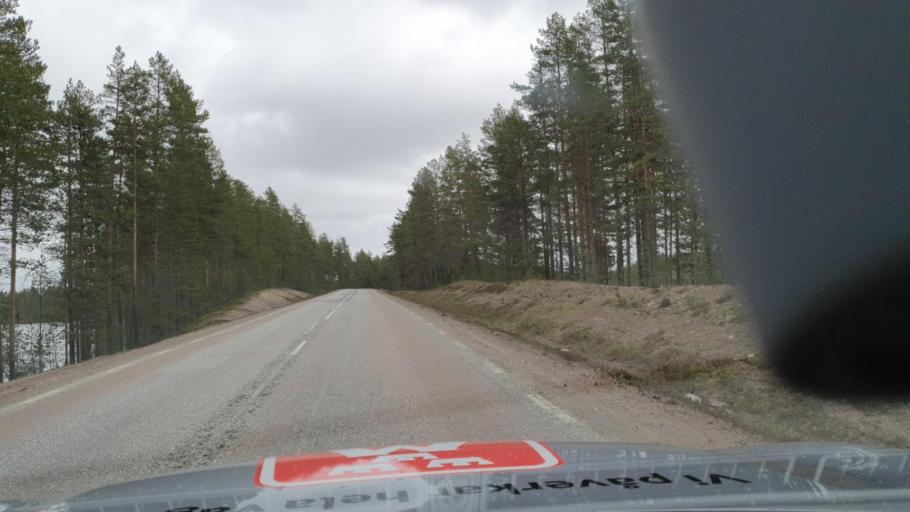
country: SE
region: Vaesternorrland
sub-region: Solleftea Kommun
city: Solleftea
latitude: 63.6496
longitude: 17.3680
